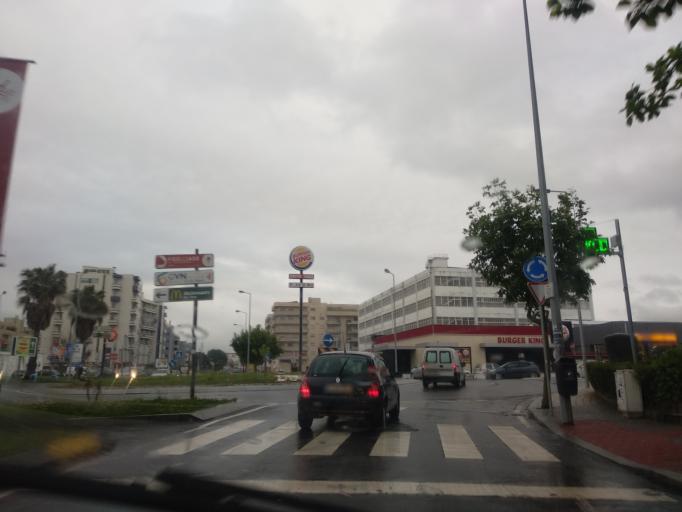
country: PT
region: Porto
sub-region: Gondomar
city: Rio Tinto
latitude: 41.1737
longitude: -8.5556
